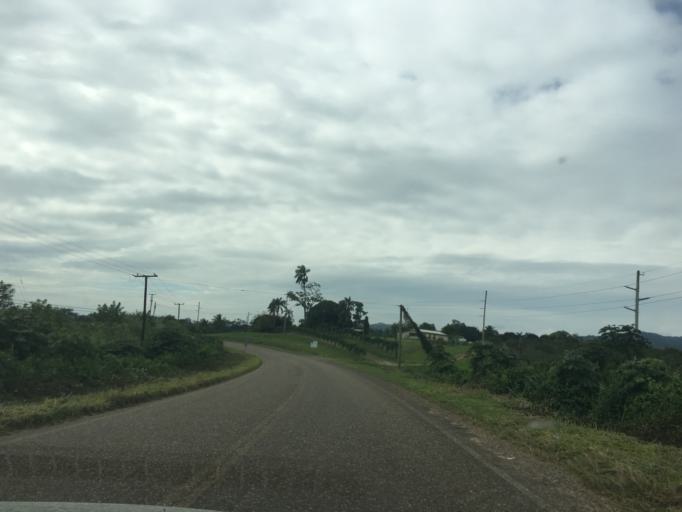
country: BZ
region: Stann Creek
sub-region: Dangriga
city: Dangriga
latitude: 16.8209
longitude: -88.3768
